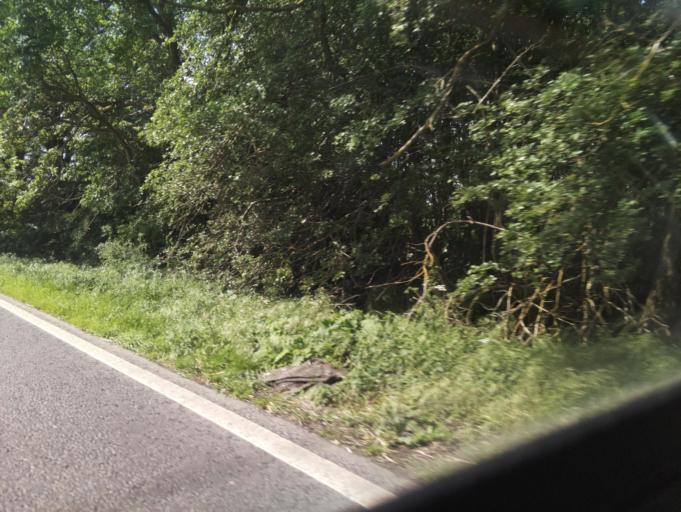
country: GB
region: England
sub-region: Lincolnshire
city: Burton
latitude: 53.3376
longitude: -0.5439
